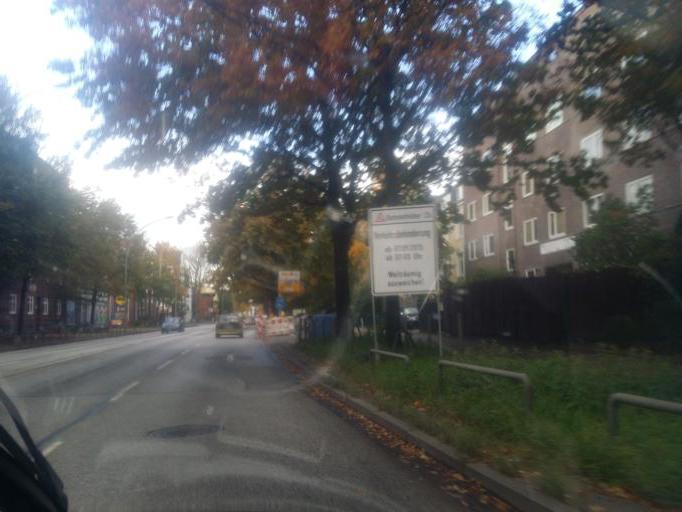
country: DE
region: Hamburg
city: Altona
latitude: 53.5646
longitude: 9.9162
